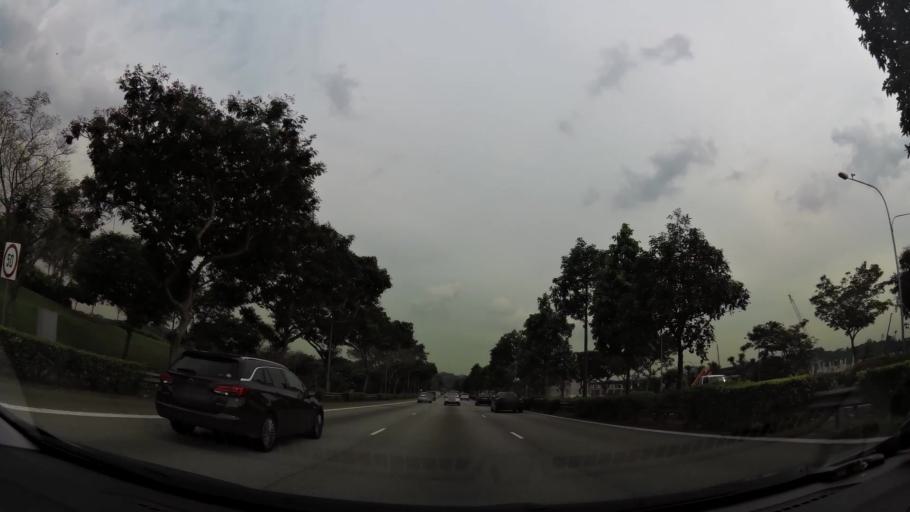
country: MY
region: Johor
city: Johor Bahru
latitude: 1.4236
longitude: 103.7933
